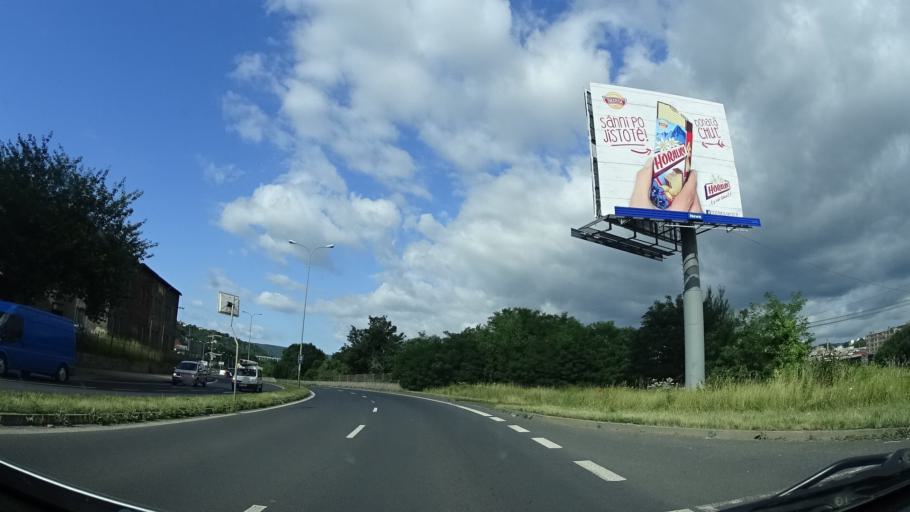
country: CZ
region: Ustecky
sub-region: Okres Usti nad Labem
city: Usti nad Labem
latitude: 50.6560
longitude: 14.0311
